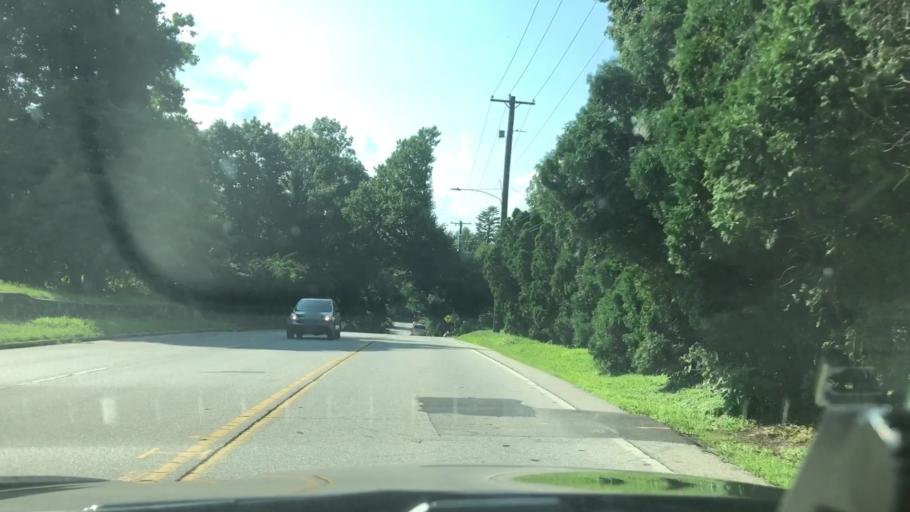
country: US
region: Pennsylvania
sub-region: Montgomery County
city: Wyndmoor
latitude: 40.0957
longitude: -75.1939
